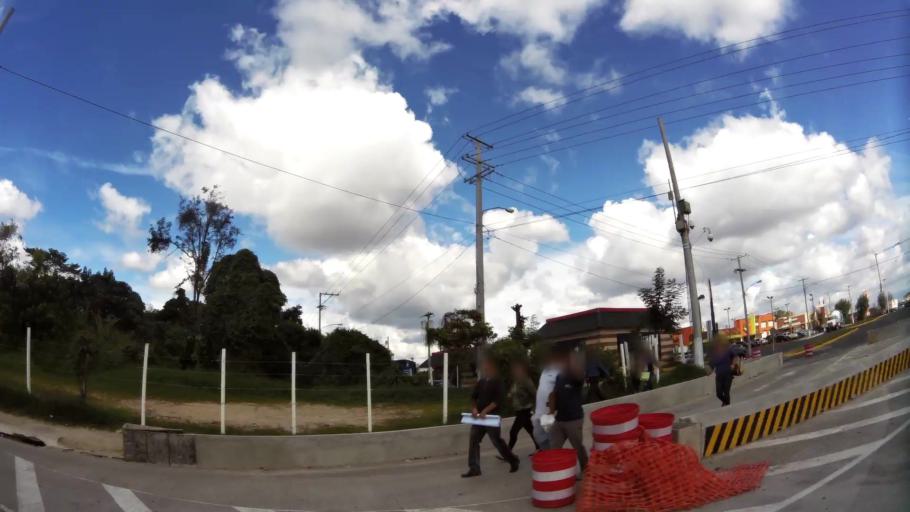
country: GT
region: Guatemala
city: Guatemala City
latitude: 14.6512
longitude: -90.5412
